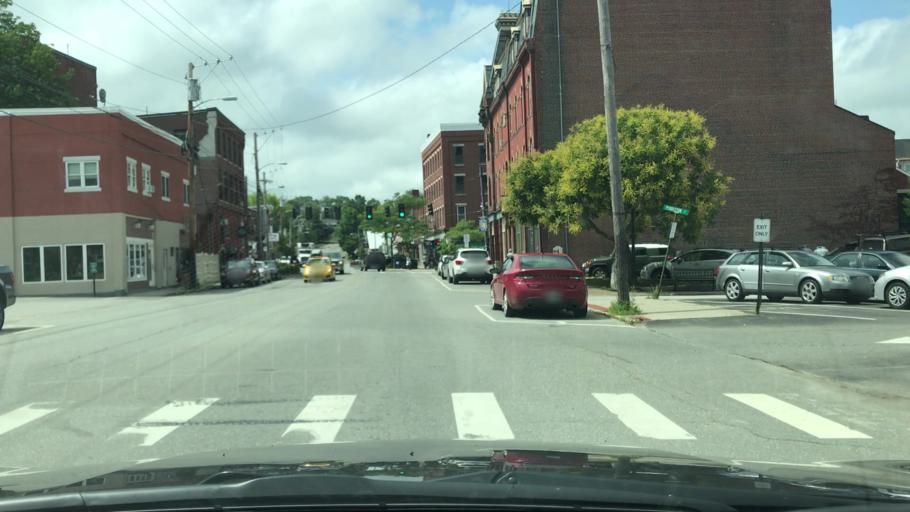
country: US
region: Maine
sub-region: Waldo County
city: Belfast
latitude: 44.4258
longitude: -69.0058
